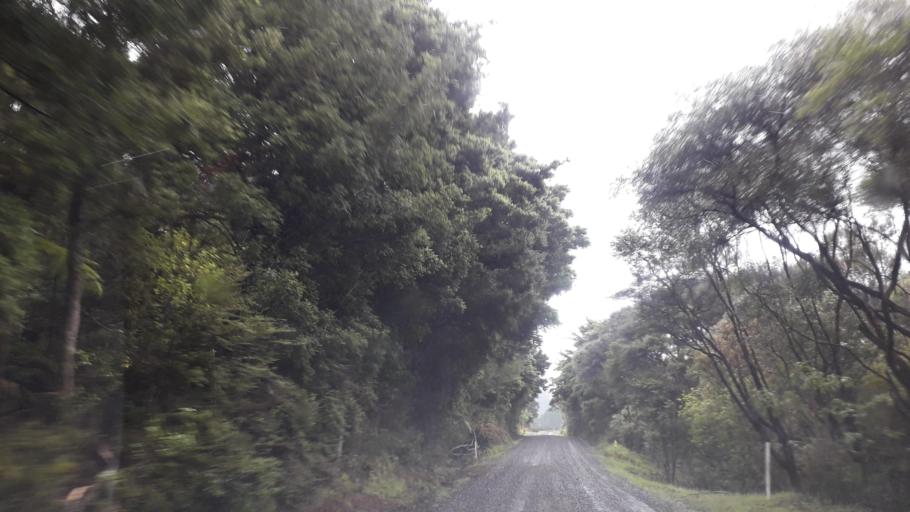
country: NZ
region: Northland
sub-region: Far North District
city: Kaitaia
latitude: -35.3899
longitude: 173.4042
